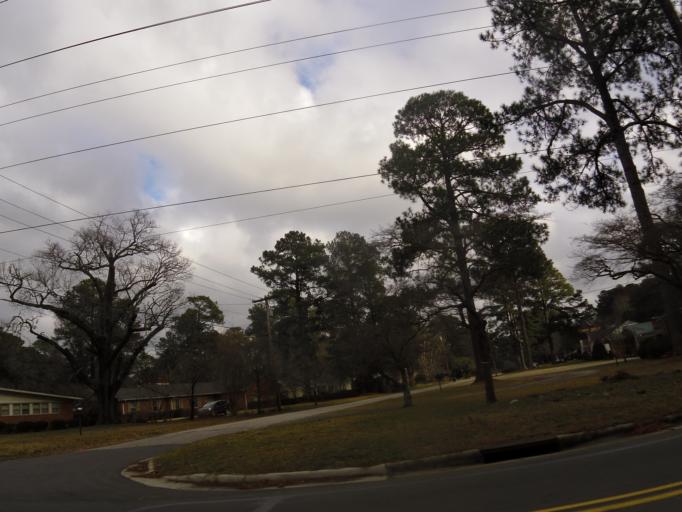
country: US
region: North Carolina
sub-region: Nash County
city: Rocky Mount
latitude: 35.9566
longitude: -77.8488
